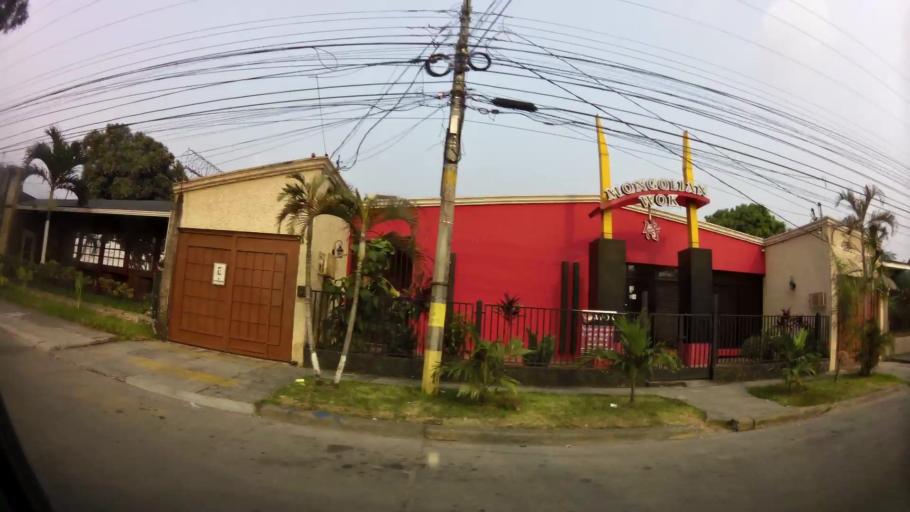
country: HN
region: Cortes
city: Armenta
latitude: 15.5017
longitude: -88.0400
